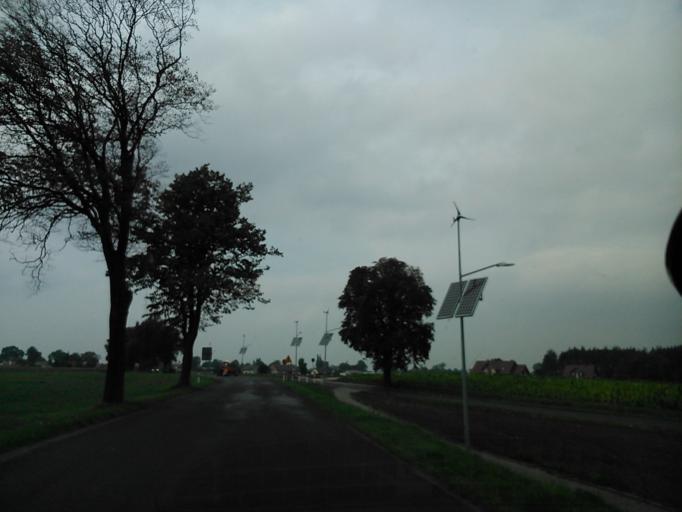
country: PL
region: Kujawsko-Pomorskie
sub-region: Powiat golubsko-dobrzynski
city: Kowalewo Pomorskie
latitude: 53.1730
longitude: 18.8623
